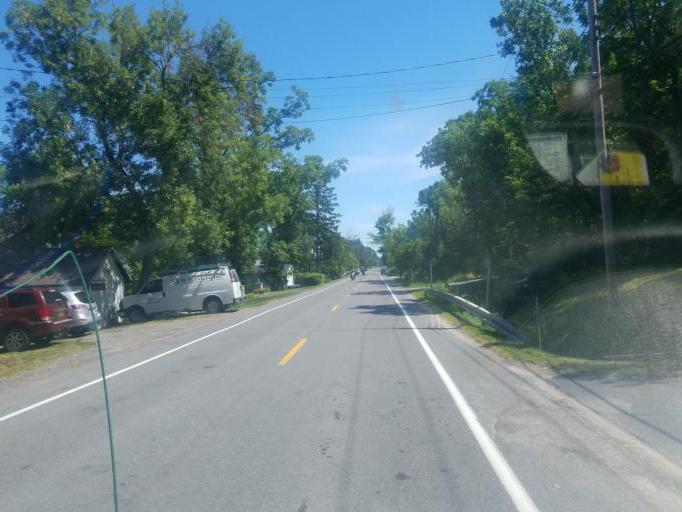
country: US
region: New York
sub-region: Ontario County
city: Canandaigua
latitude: 42.7844
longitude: -77.2829
